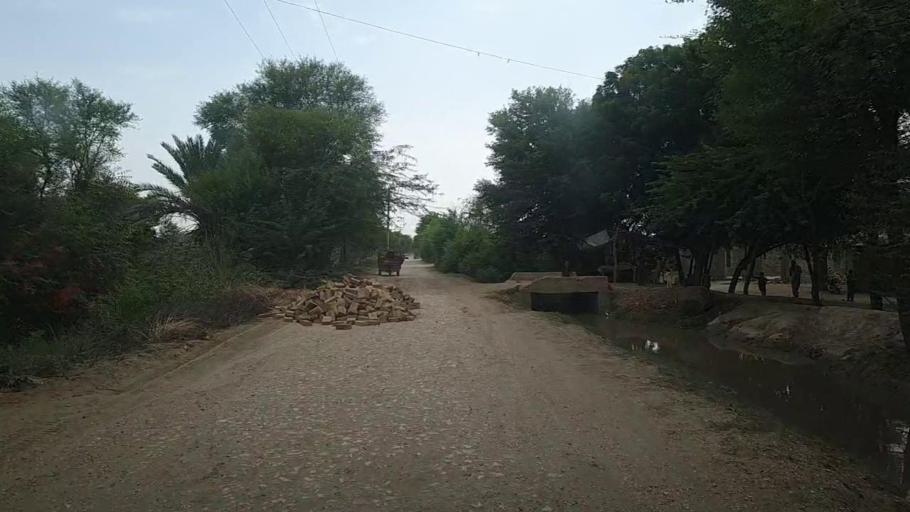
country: PK
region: Sindh
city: Karaundi
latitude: 26.9536
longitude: 68.4163
